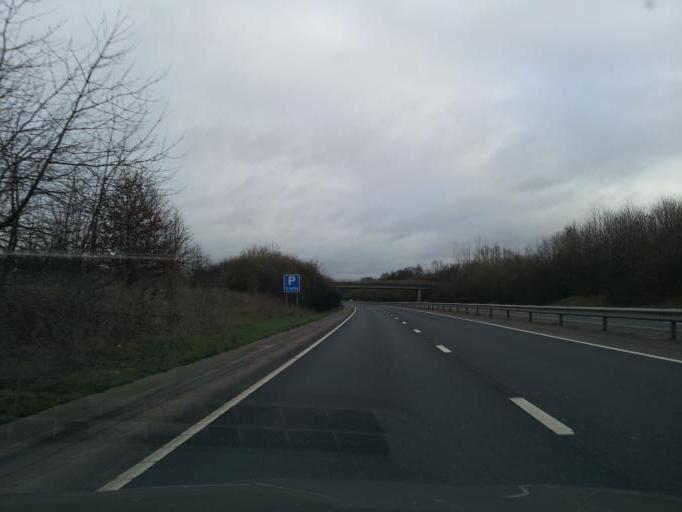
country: GB
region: England
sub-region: Norfolk
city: Diss
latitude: 52.3714
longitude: 1.1606
